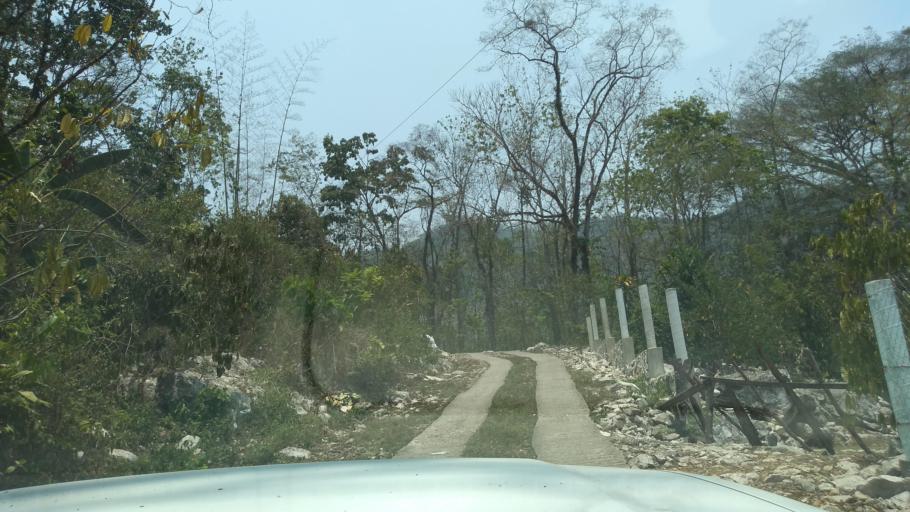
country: MX
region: Veracruz
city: Cosolapa
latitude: 18.5968
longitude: -96.7276
